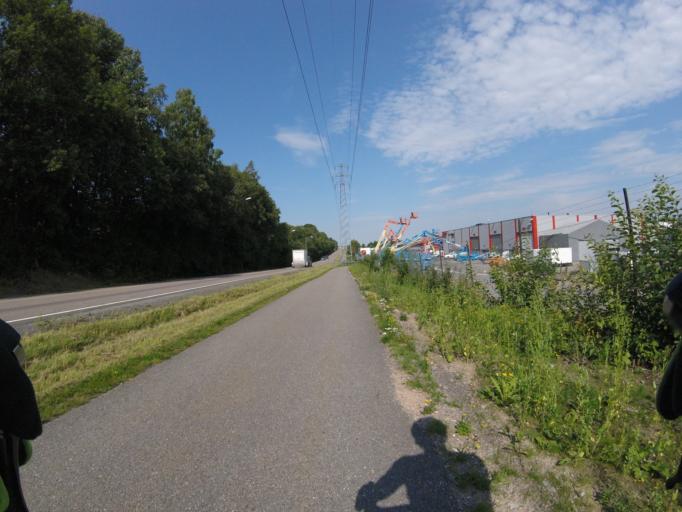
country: NO
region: Akershus
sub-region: Skedsmo
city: Lillestrom
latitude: 59.9688
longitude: 11.0660
